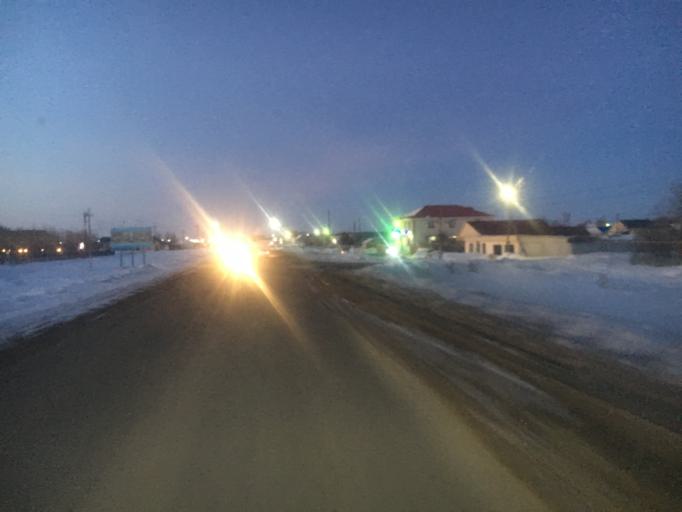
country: KZ
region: Batys Qazaqstan
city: Oral
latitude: 51.1494
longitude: 51.4888
